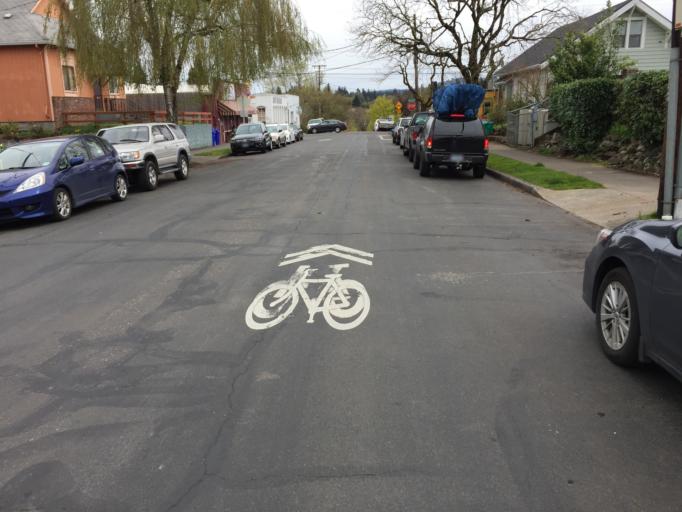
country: US
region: Oregon
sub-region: Clackamas County
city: Milwaukie
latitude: 45.4650
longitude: -122.6479
